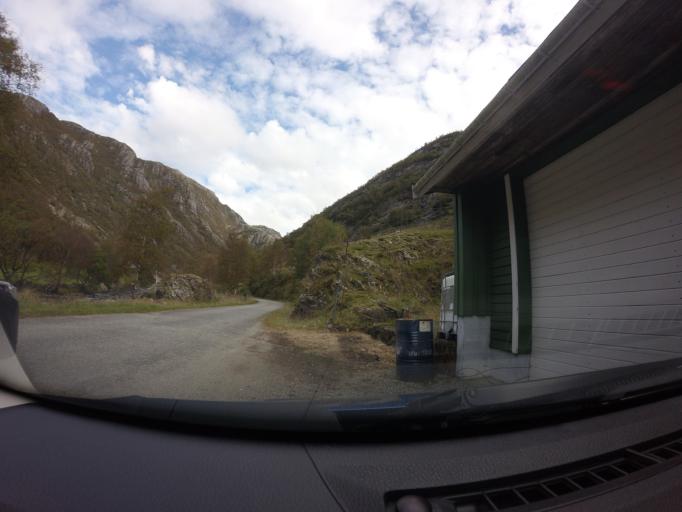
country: NO
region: Rogaland
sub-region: Forsand
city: Forsand
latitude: 58.8548
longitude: 6.3727
